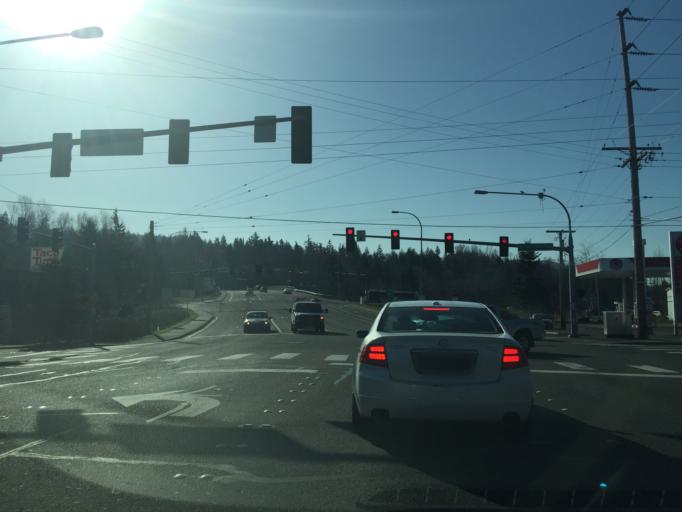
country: US
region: Washington
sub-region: Whatcom County
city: Bellingham
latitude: 48.7340
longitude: -122.4699
